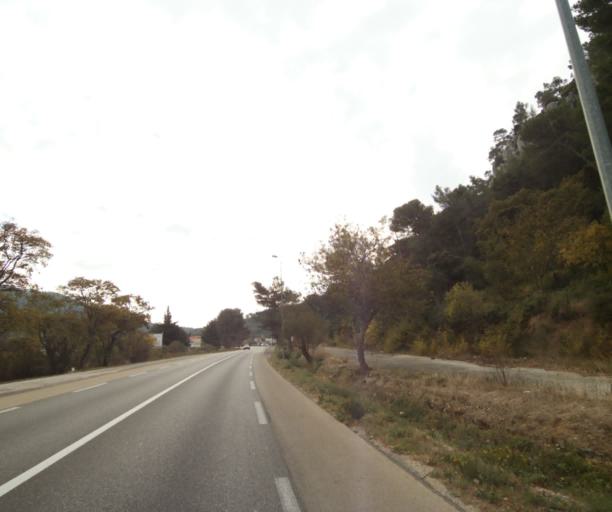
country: FR
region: Provence-Alpes-Cote d'Azur
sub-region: Departement des Bouches-du-Rhone
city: Gemenos
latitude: 43.2762
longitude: 5.6311
